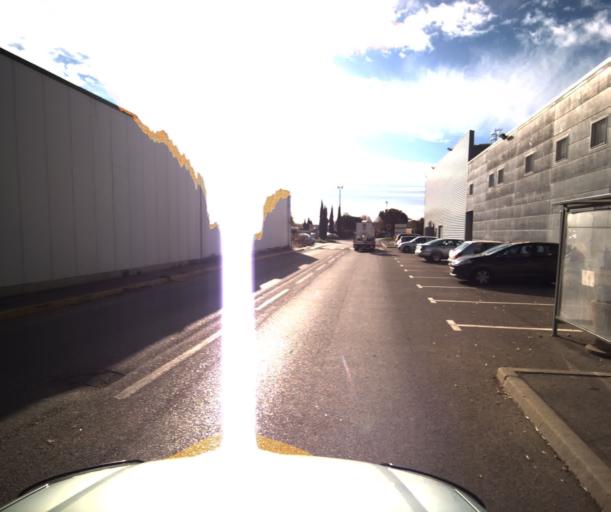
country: FR
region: Provence-Alpes-Cote d'Azur
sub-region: Departement du Vaucluse
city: Pertuis
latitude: 43.6813
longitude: 5.5024
